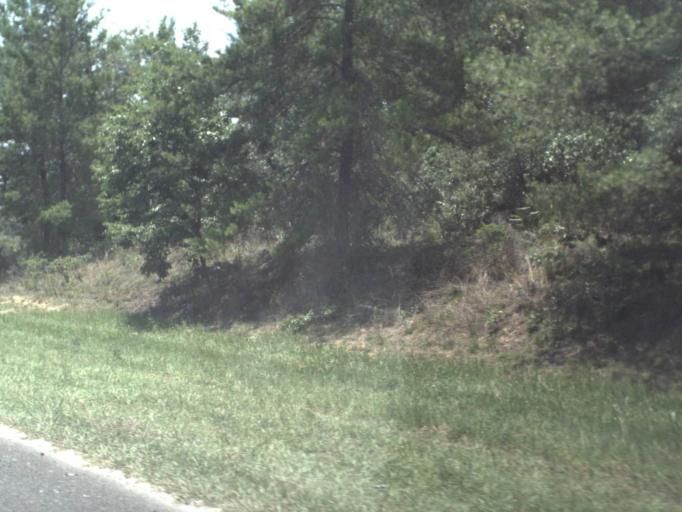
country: US
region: Florida
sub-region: Putnam County
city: Crescent City
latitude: 29.4345
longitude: -81.7376
